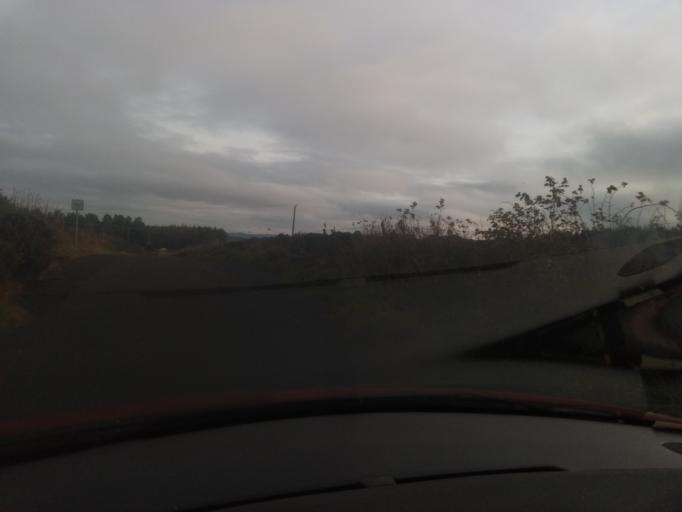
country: GB
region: Scotland
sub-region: The Scottish Borders
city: Jedburgh
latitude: 55.4828
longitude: -2.5803
